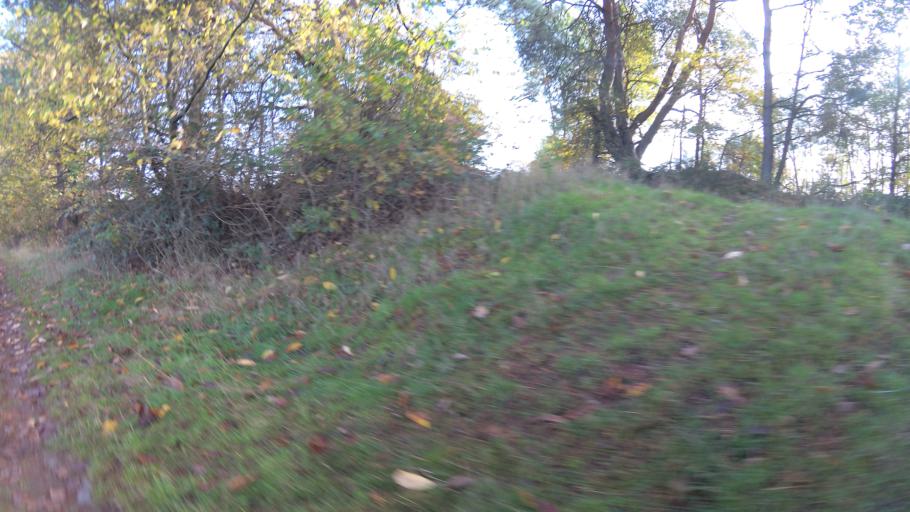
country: DE
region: Saarland
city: Bexbach
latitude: 49.3478
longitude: 7.2814
